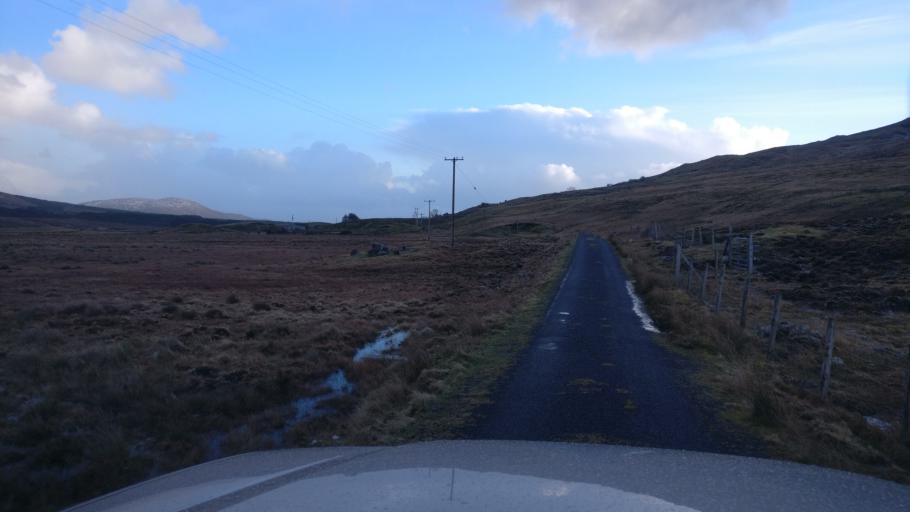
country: IE
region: Connaught
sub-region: County Galway
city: Clifden
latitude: 53.4944
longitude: -9.7037
